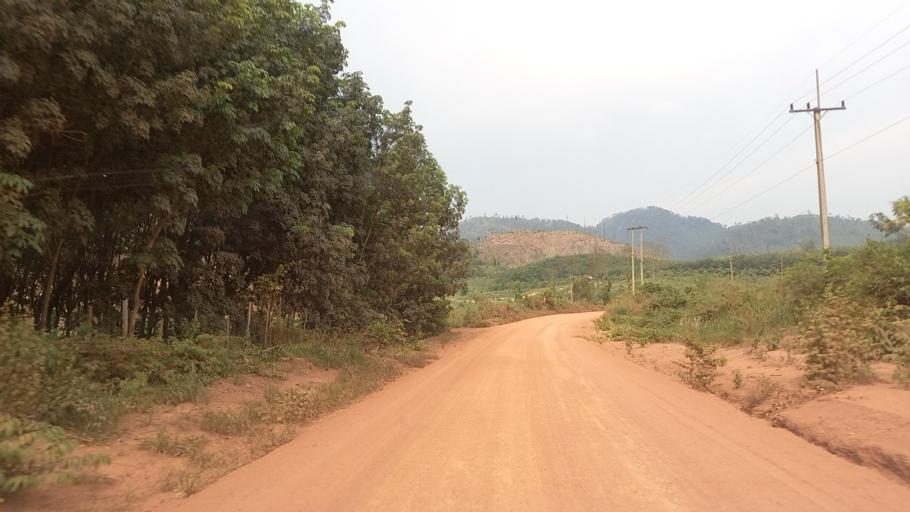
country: LA
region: Bolikhamxai
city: Bolikhan
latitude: 18.5358
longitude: 103.8151
